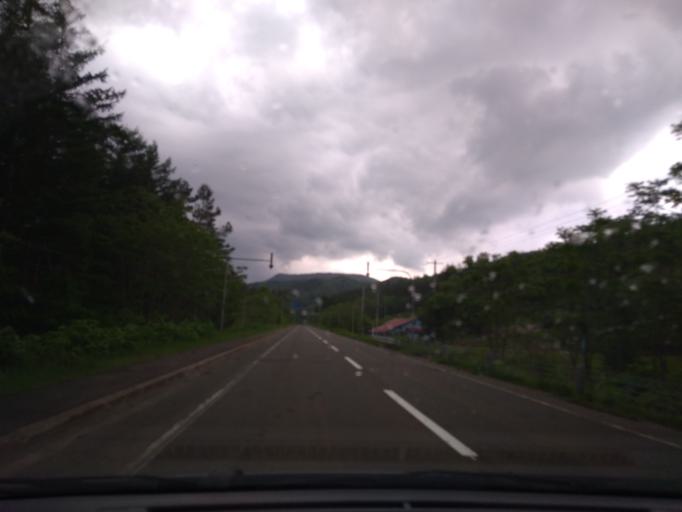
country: JP
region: Hokkaido
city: Shimo-furano
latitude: 43.1277
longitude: 142.4118
